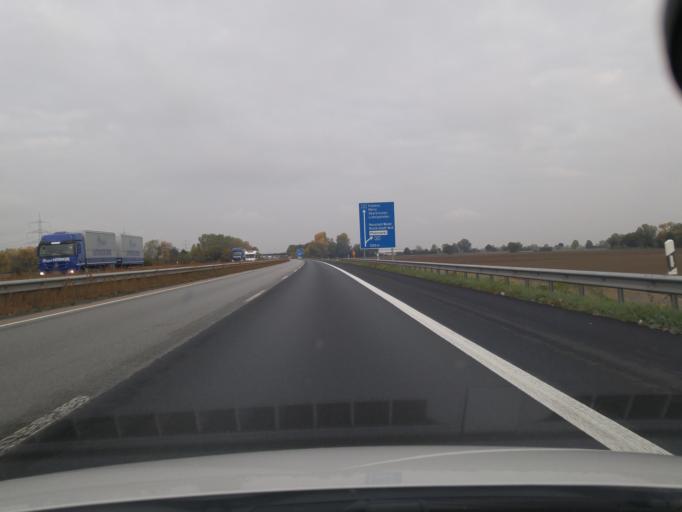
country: DE
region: Rheinland-Pfalz
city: Mutterstadt
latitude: 49.4239
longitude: 8.3372
